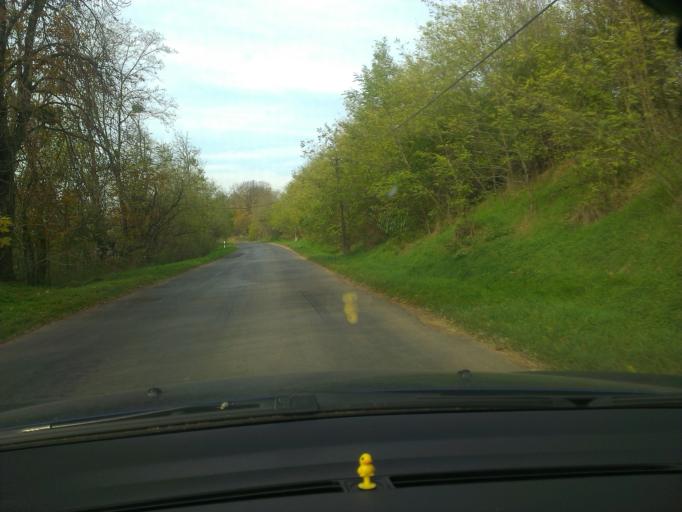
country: HU
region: Gyor-Moson-Sopron
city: Bakonyszentlaszlo
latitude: 47.3996
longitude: 17.8251
